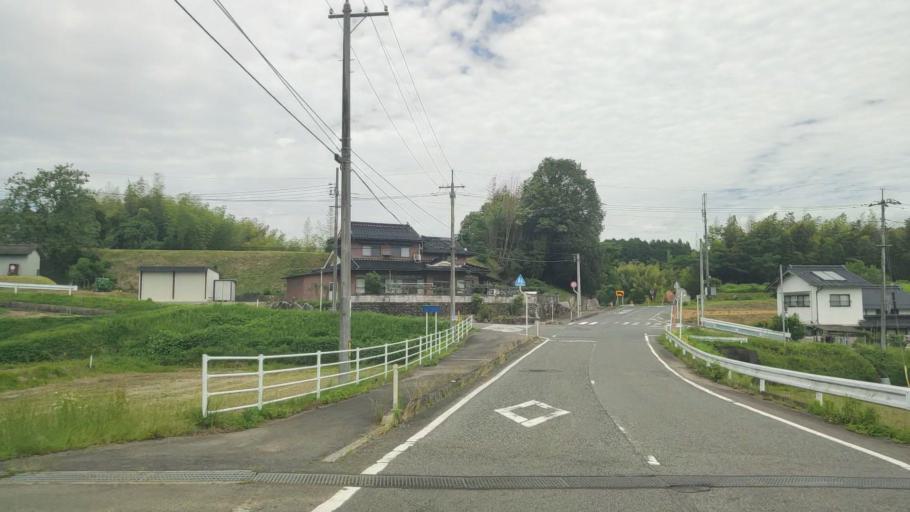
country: JP
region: Hyogo
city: Yamazakicho-nakabirose
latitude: 35.0930
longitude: 134.2864
